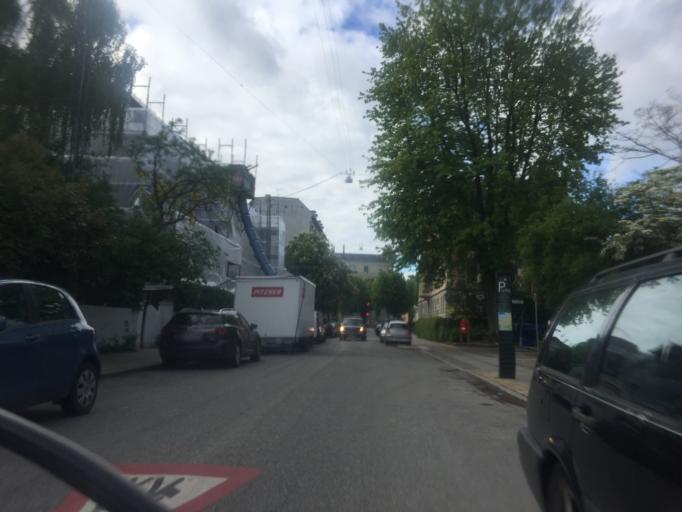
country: DK
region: Capital Region
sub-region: Frederiksberg Kommune
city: Frederiksberg
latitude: 55.6754
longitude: 12.5379
